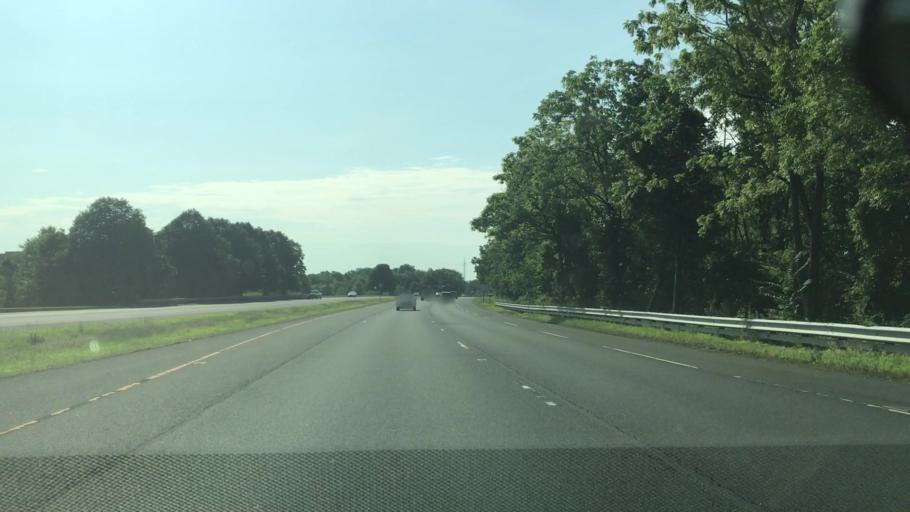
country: US
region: New Jersey
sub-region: Somerset County
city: Bridgewater
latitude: 40.5872
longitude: -74.6370
